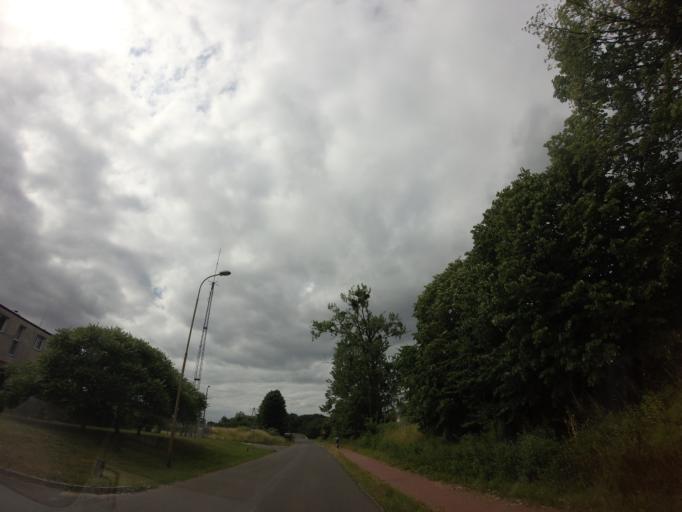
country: PL
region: Lubusz
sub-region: Powiat strzelecko-drezdenecki
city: Strzelce Krajenskie
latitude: 52.8688
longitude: 15.5279
